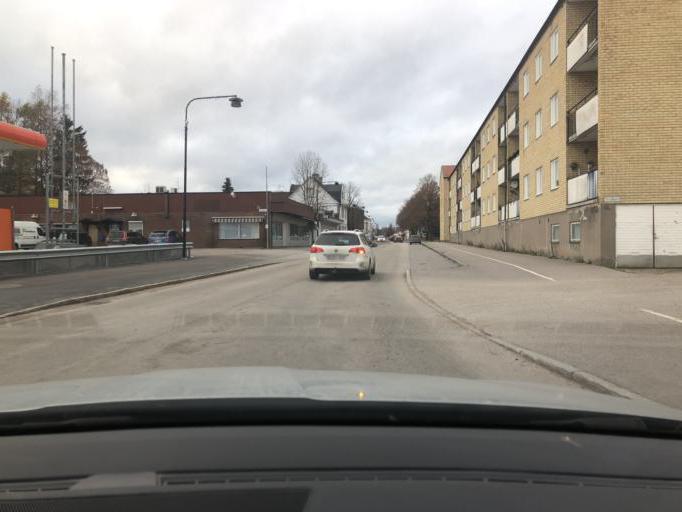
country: SE
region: Uppsala
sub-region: Tierps Kommun
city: Tierp
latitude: 60.3415
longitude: 17.5193
